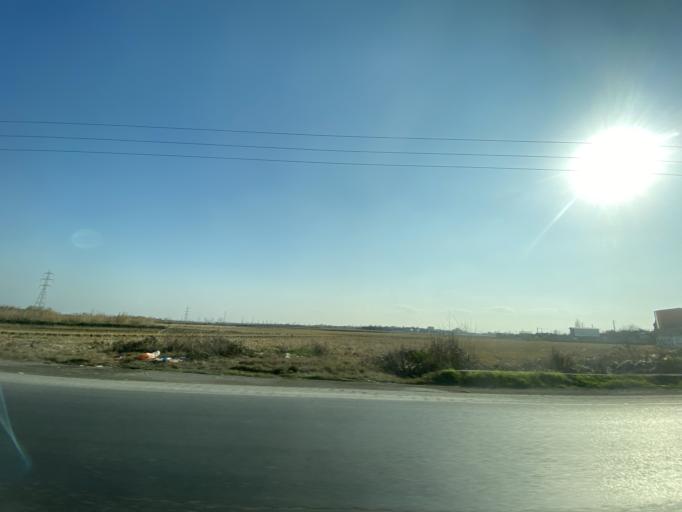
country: IR
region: Mazandaran
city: Babol
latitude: 36.5127
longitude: 52.5608
